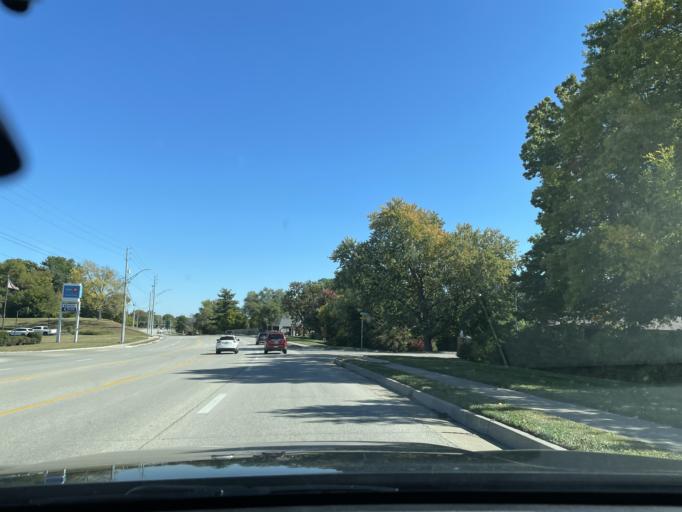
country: US
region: Missouri
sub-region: Buchanan County
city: Saint Joseph
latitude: 39.7770
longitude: -94.7913
